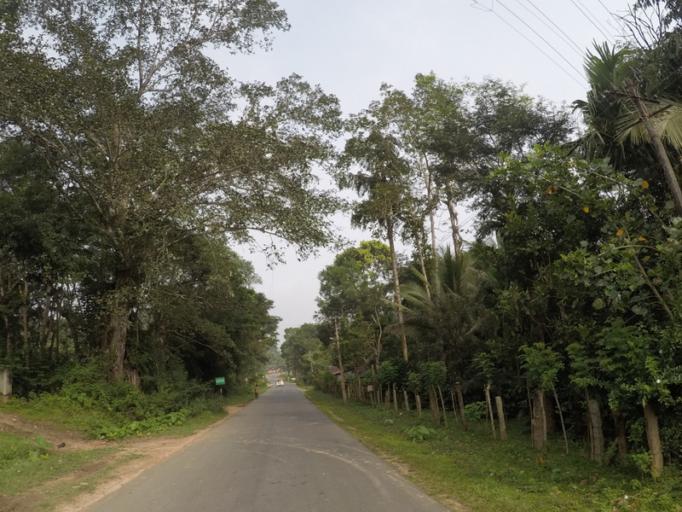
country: IN
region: Karnataka
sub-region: Chikmagalur
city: Chikmagalur
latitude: 13.3379
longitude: 75.5482
